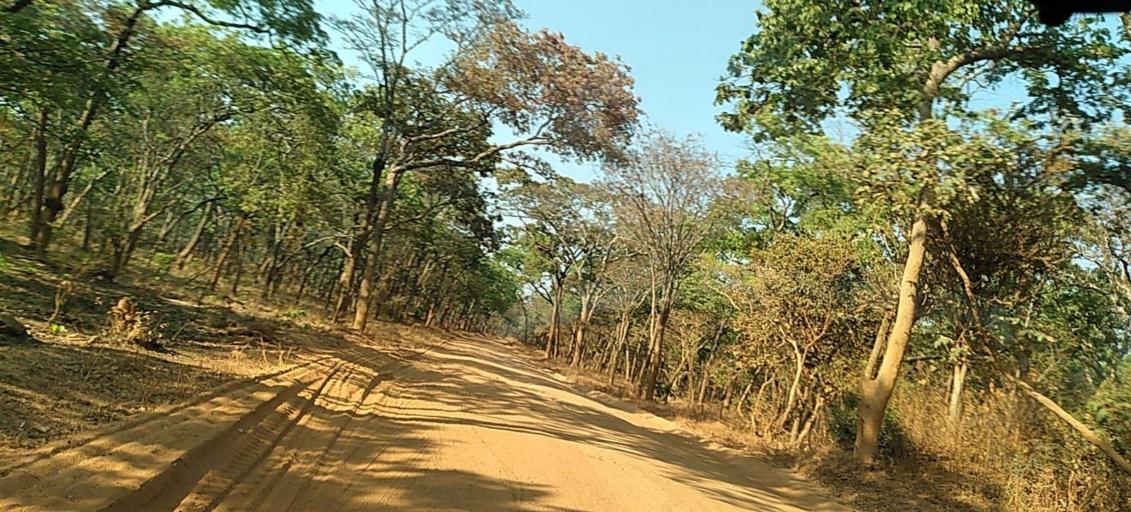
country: ZM
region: North-Western
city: Kasempa
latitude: -13.5849
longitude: 25.9869
